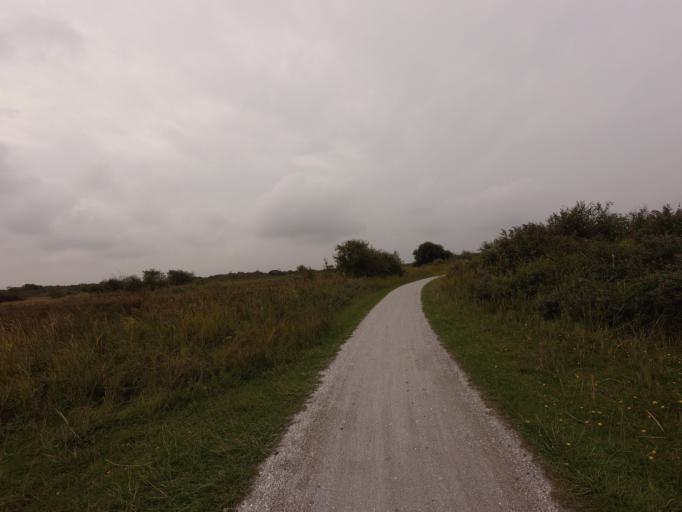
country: NL
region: Friesland
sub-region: Gemeente Schiermonnikoog
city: Schiermonnikoog
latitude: 53.4892
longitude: 6.2027
